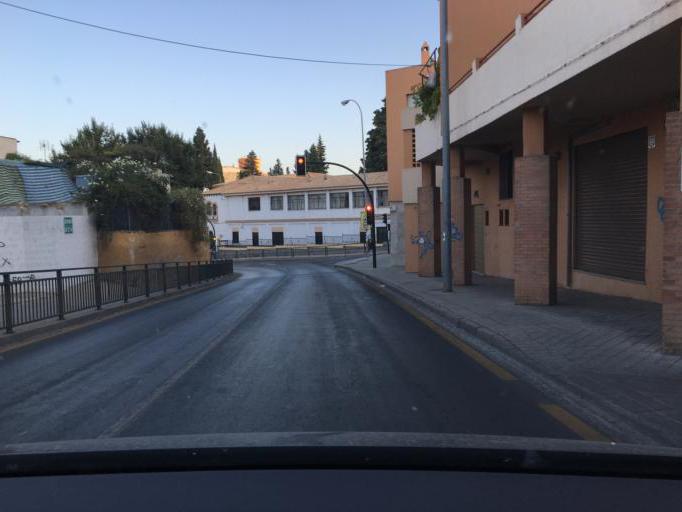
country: ES
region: Andalusia
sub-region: Provincia de Granada
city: Granada
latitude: 37.1875
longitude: -3.5991
